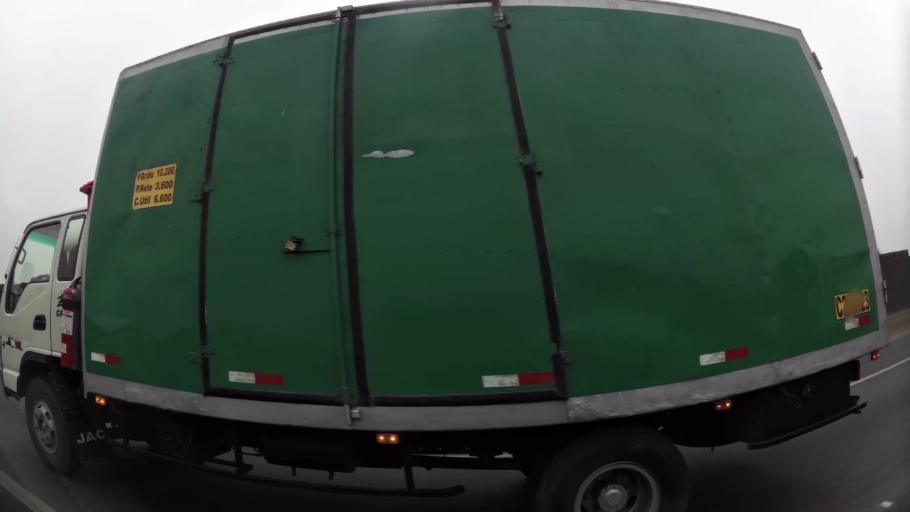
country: PE
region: Lima
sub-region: Lima
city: Santa Maria
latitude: -12.0173
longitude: -76.9090
